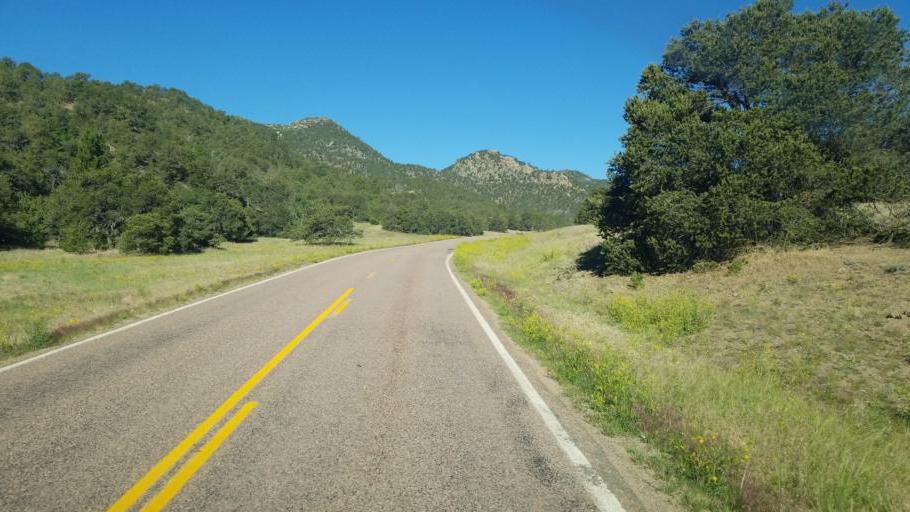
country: US
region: Colorado
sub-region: Fremont County
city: Canon City
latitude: 38.4121
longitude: -105.4254
